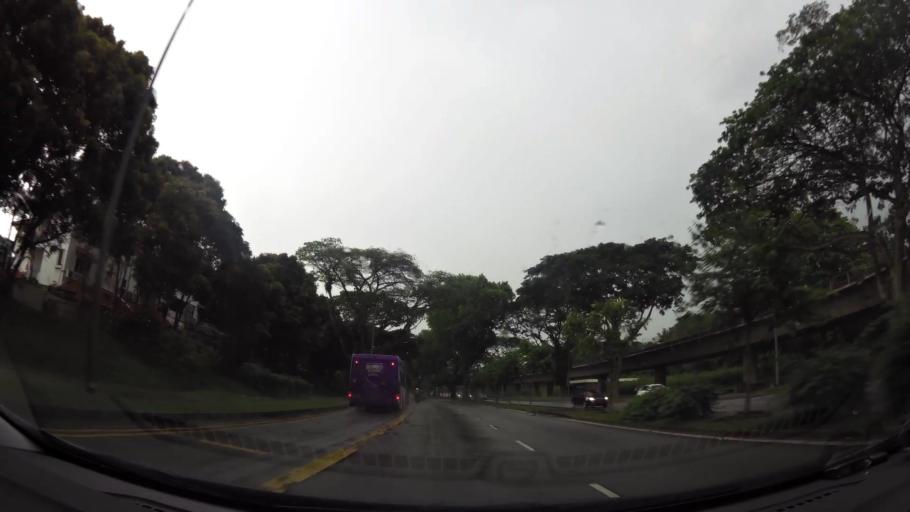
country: MY
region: Johor
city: Kampung Pasir Gudang Baru
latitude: 1.3904
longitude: 103.8399
